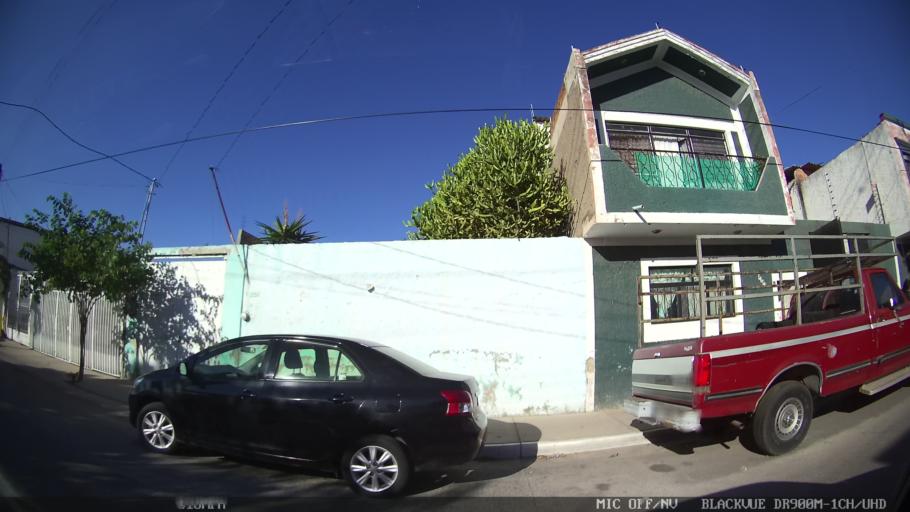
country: MX
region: Jalisco
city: Tlaquepaque
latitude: 20.7092
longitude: -103.2982
